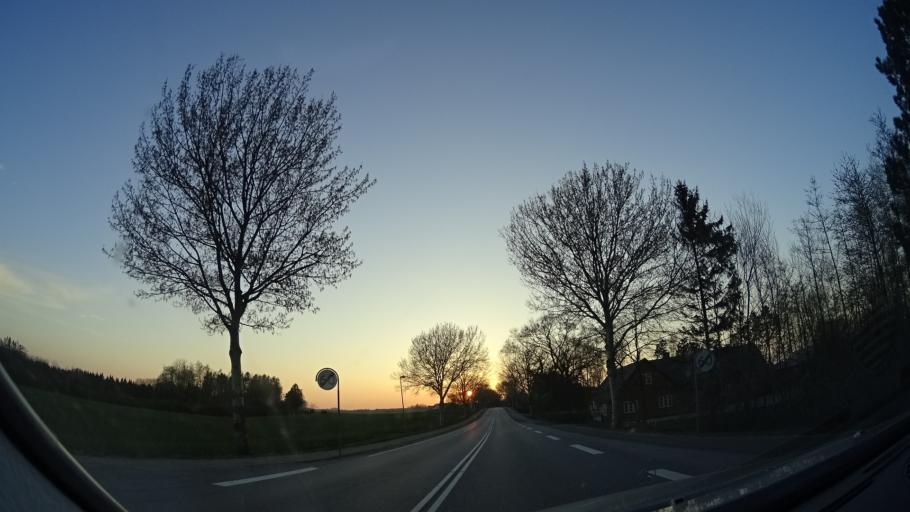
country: DK
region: Zealand
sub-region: Solrod Kommune
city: Solrod
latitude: 55.5541
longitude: 12.1570
